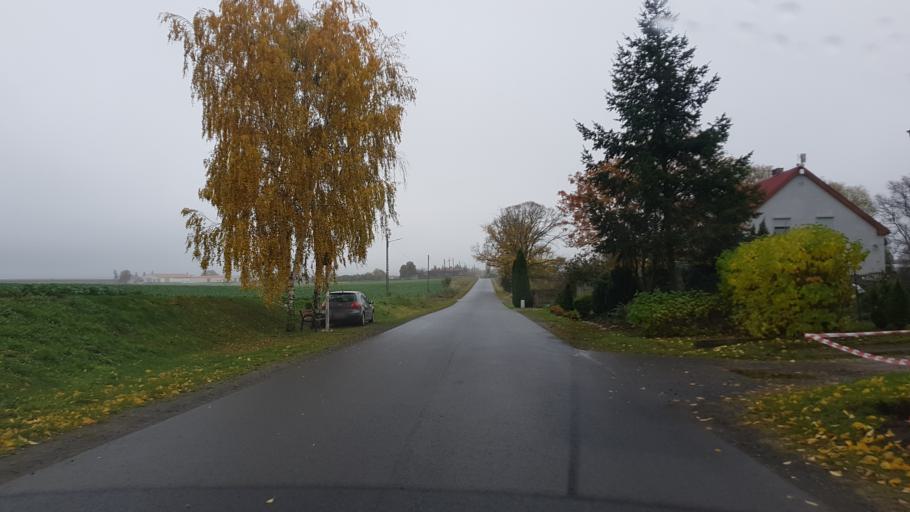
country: PL
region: West Pomeranian Voivodeship
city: Trzcinsko Zdroj
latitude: 53.0672
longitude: 14.5331
